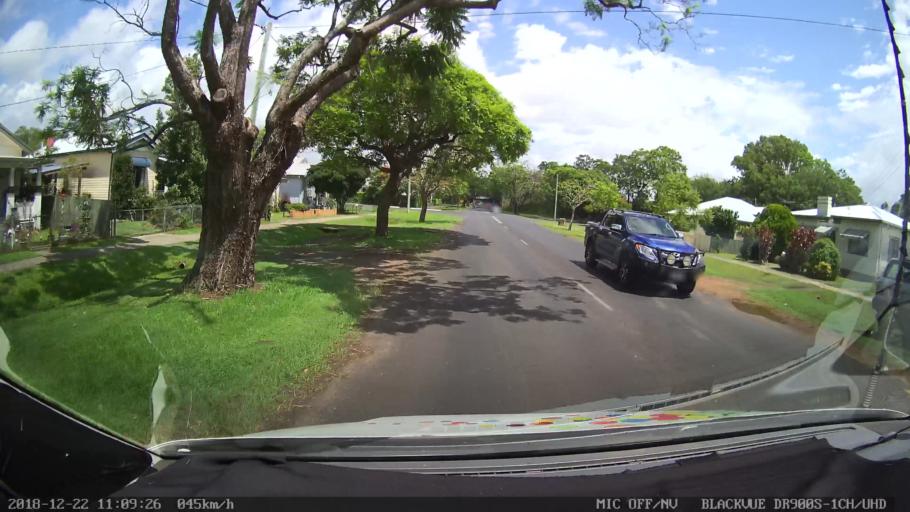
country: AU
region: New South Wales
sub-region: Clarence Valley
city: Grafton
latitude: -29.6859
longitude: 152.9289
